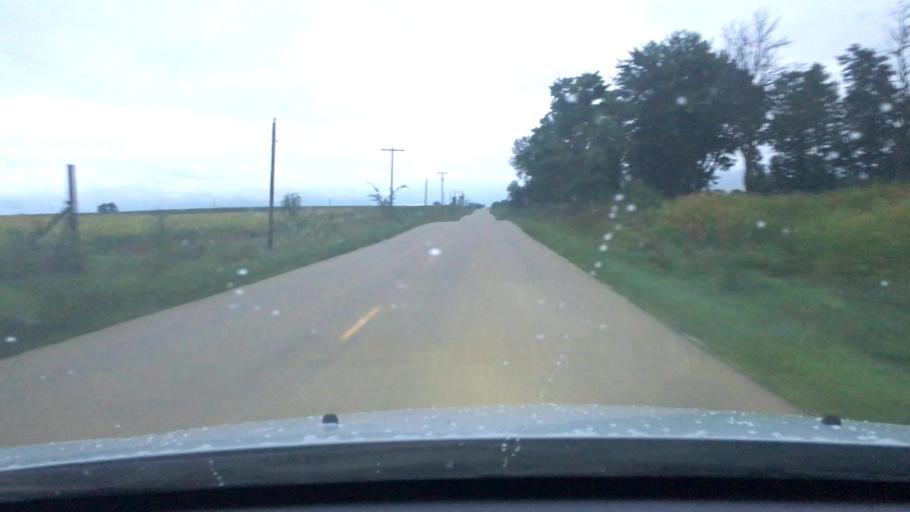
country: US
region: Illinois
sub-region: DeKalb County
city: Malta
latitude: 41.8661
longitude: -88.9615
